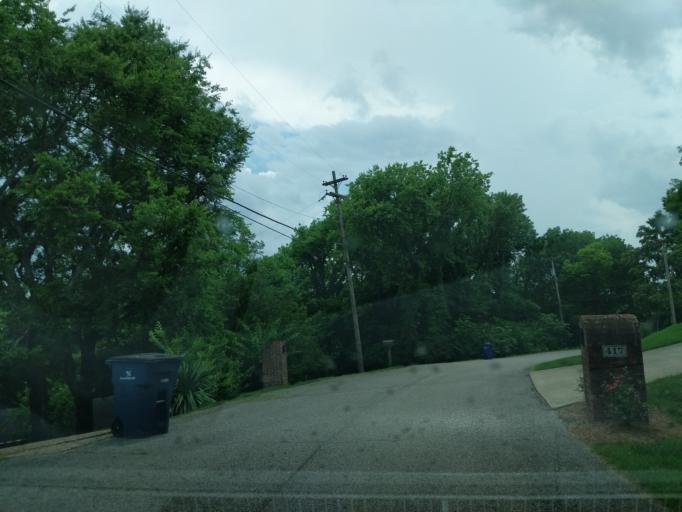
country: US
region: Tennessee
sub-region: Davidson County
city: Goodlettsville
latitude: 36.3133
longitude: -86.7280
